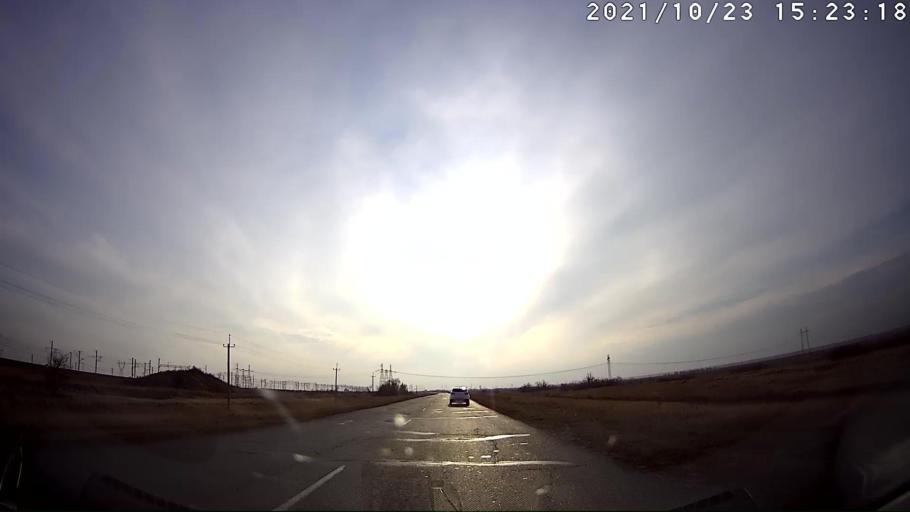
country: RU
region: Volgograd
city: Bereslavka
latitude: 48.2985
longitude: 44.2874
